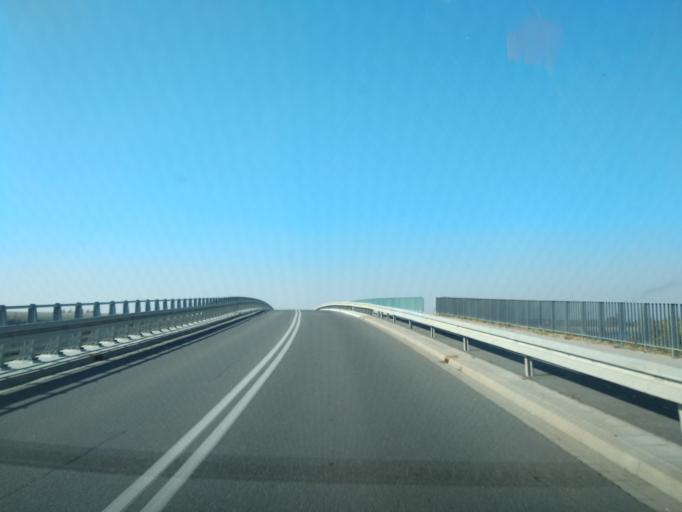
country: PL
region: Lower Silesian Voivodeship
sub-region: Powiat wroclawski
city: Smolec
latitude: 51.0733
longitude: 16.9286
